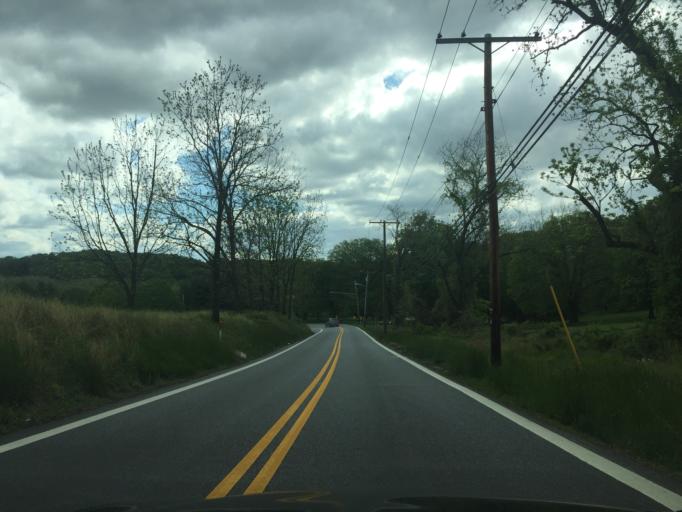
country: US
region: Maryland
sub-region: Baltimore County
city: Mays Chapel
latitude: 39.3962
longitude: -76.6730
